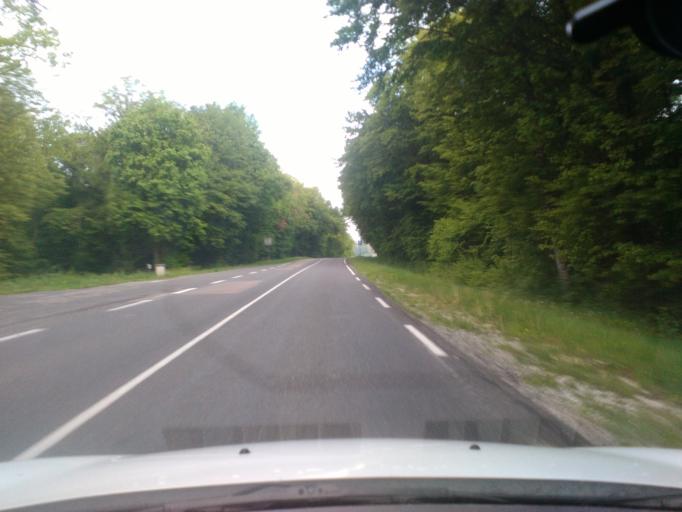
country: FR
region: Champagne-Ardenne
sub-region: Departement de la Haute-Marne
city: Lavilleneuve-au-Roi
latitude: 48.2141
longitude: 4.9119
